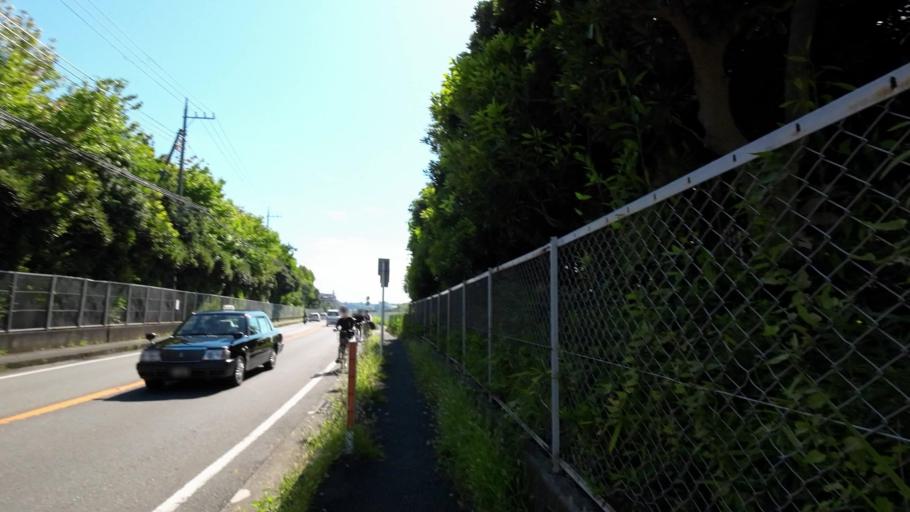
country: JP
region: Kanagawa
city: Fujisawa
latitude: 35.3460
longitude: 139.5122
